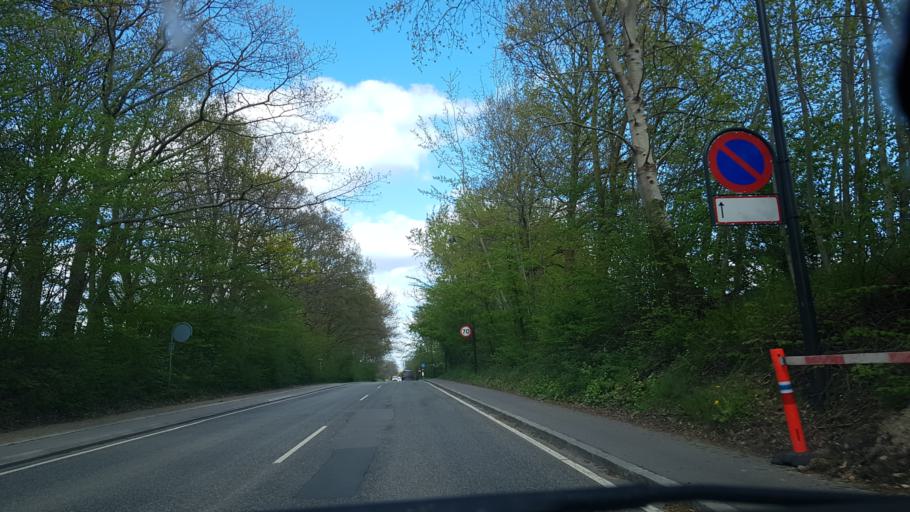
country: DK
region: Capital Region
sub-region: Rudersdal Kommune
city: Trorod
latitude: 55.8253
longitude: 12.5073
